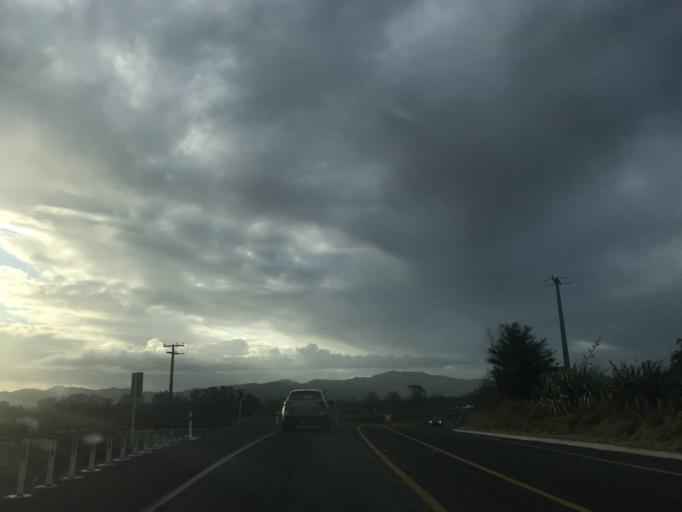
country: NZ
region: Bay of Plenty
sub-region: Western Bay of Plenty District
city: Waihi Beach
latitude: -37.4449
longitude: 175.8774
